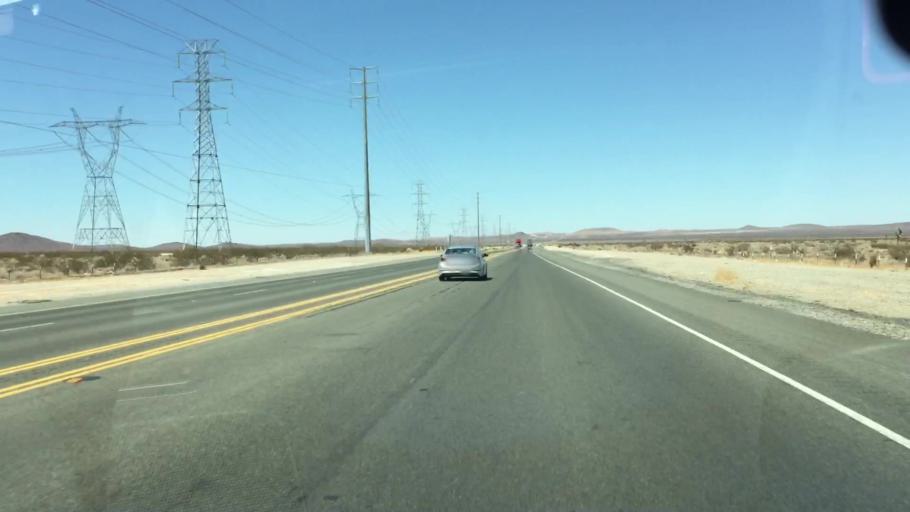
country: US
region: California
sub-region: San Bernardino County
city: Adelanto
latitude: 34.7756
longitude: -117.4790
